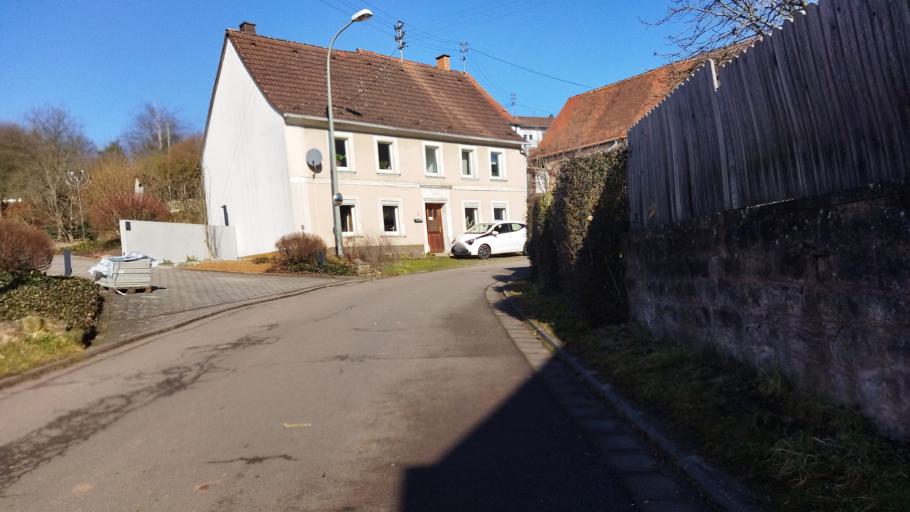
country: DE
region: Rheinland-Pfalz
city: Rehweiler
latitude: 49.4865
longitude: 7.4394
